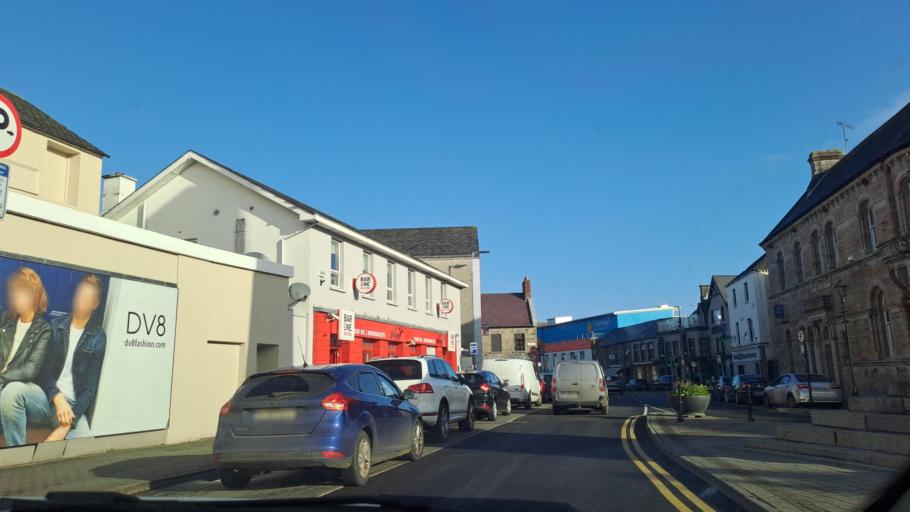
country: IE
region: Ulster
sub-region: County Monaghan
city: Monaghan
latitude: 54.2478
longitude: -6.9709
